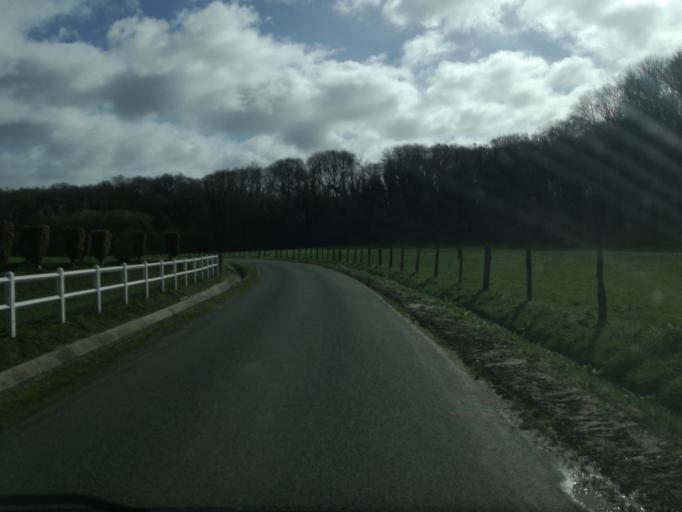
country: FR
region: Haute-Normandie
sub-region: Departement de la Seine-Maritime
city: Bretteville-du-Grand-Caux
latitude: 49.6980
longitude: 0.4629
